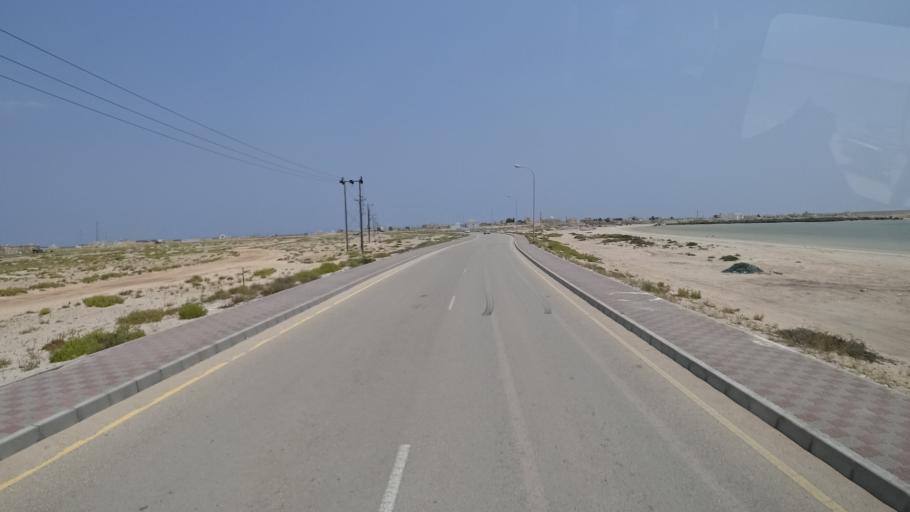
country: OM
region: Ash Sharqiyah
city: Sur
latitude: 22.5280
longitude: 59.7812
